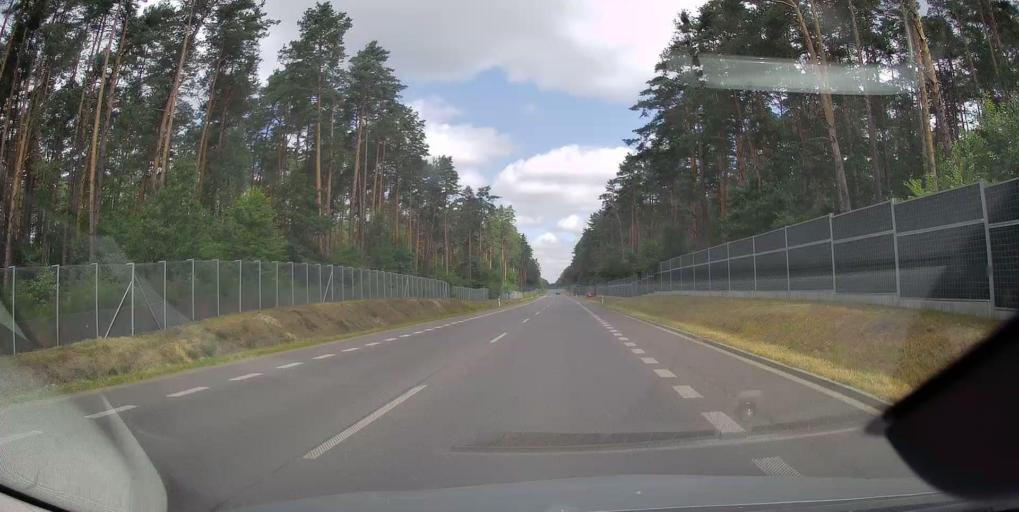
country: PL
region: Subcarpathian Voivodeship
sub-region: Powiat mielecki
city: Mielec
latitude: 50.2674
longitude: 21.4946
